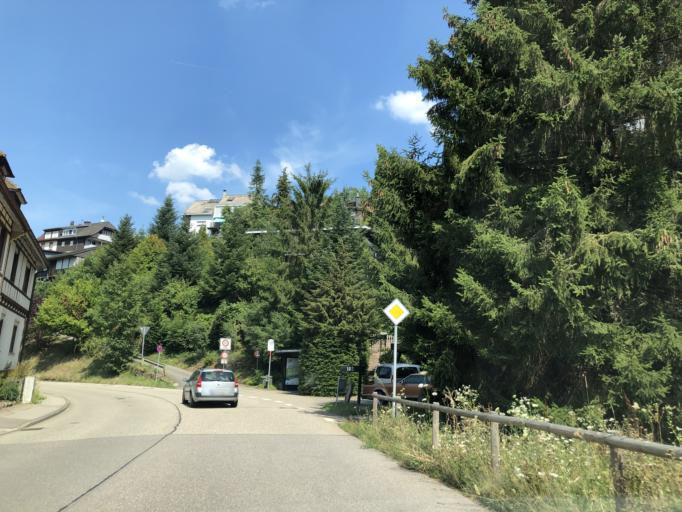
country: DE
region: Baden-Wuerttemberg
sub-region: Karlsruhe Region
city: Baden-Baden
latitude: 48.7319
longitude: 8.2570
